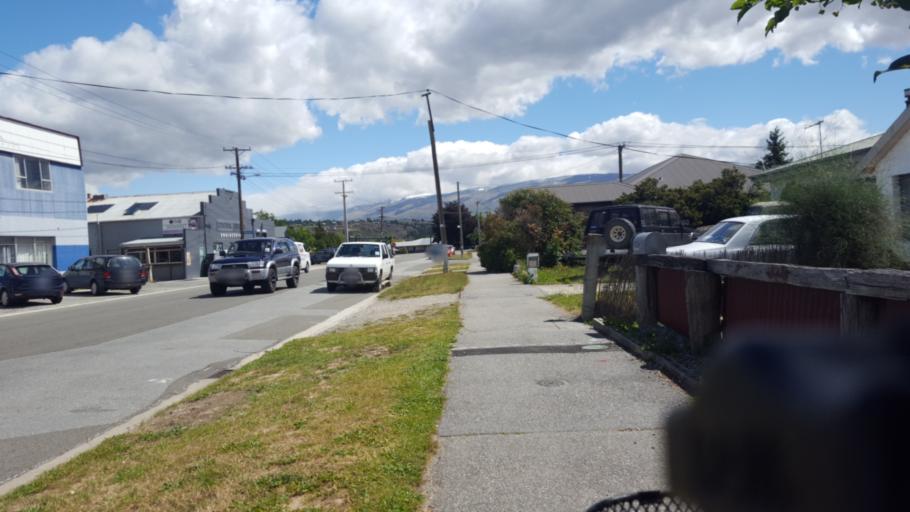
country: NZ
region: Otago
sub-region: Queenstown-Lakes District
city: Wanaka
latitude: -45.2468
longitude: 169.3932
